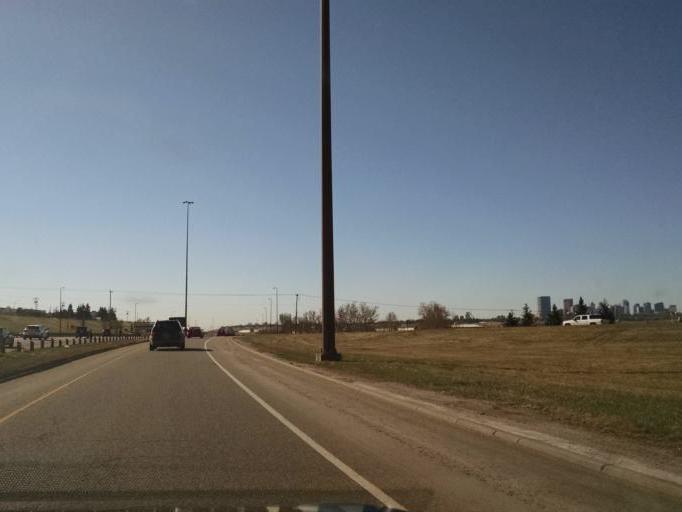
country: CA
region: Alberta
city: Calgary
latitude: 51.0952
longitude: -114.0407
